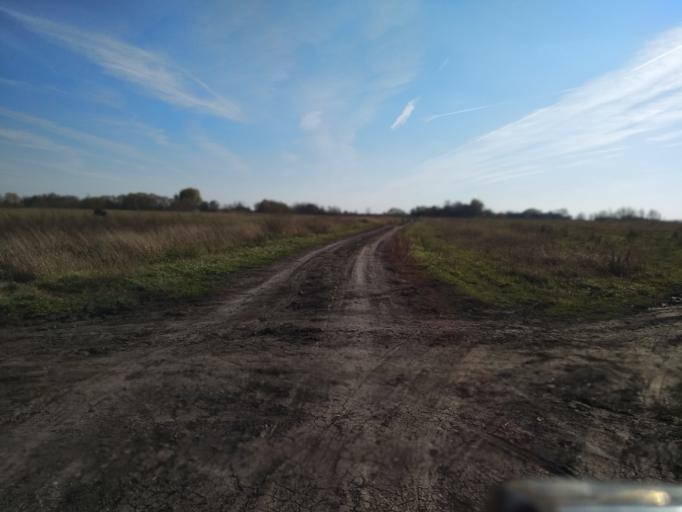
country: RU
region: Lipetsk
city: Dobrinka
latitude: 52.0276
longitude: 40.5554
